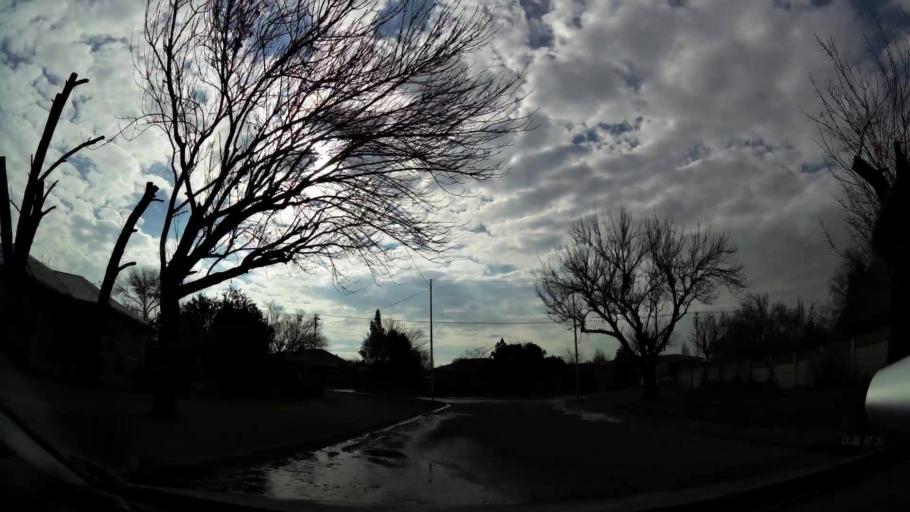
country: ZA
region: Orange Free State
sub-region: Mangaung Metropolitan Municipality
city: Bloemfontein
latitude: -29.0826
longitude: 26.2413
